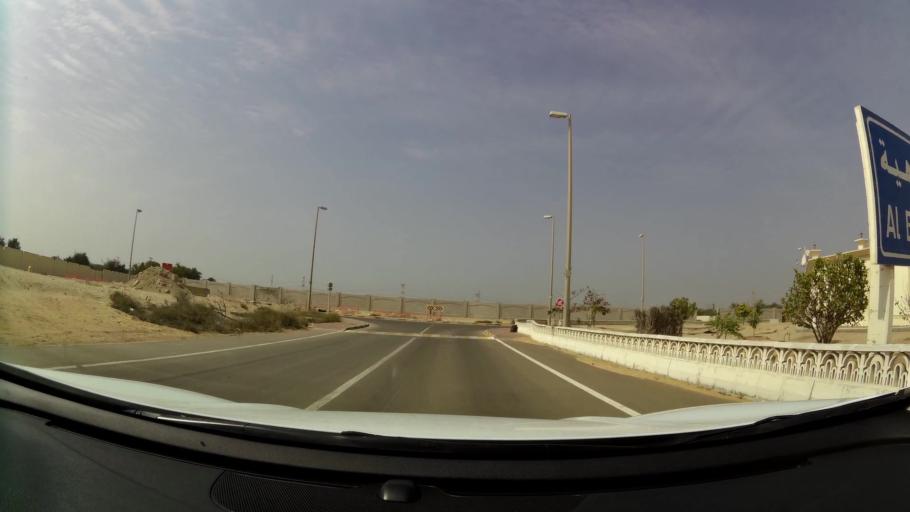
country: AE
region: Abu Dhabi
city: Abu Dhabi
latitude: 24.5448
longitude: 54.6610
